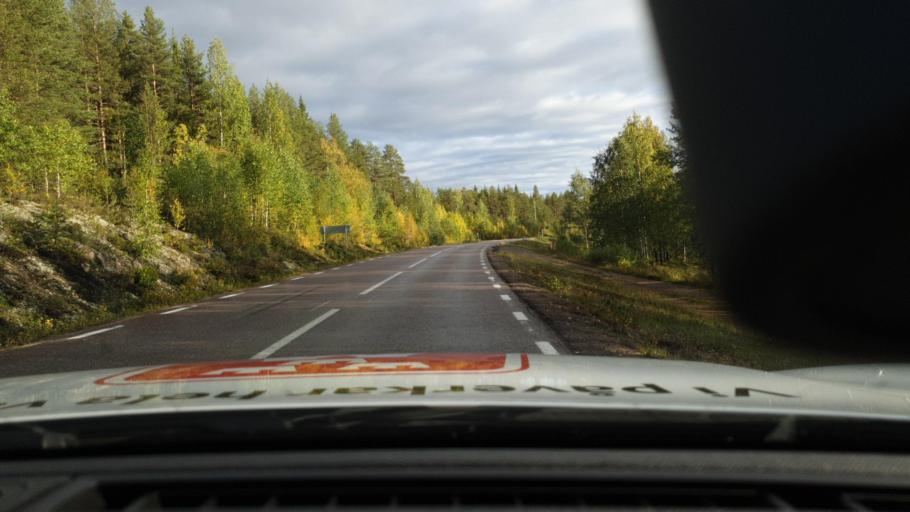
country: SE
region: Norrbotten
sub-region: Overkalix Kommun
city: OEverkalix
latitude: 66.6515
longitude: 22.7168
